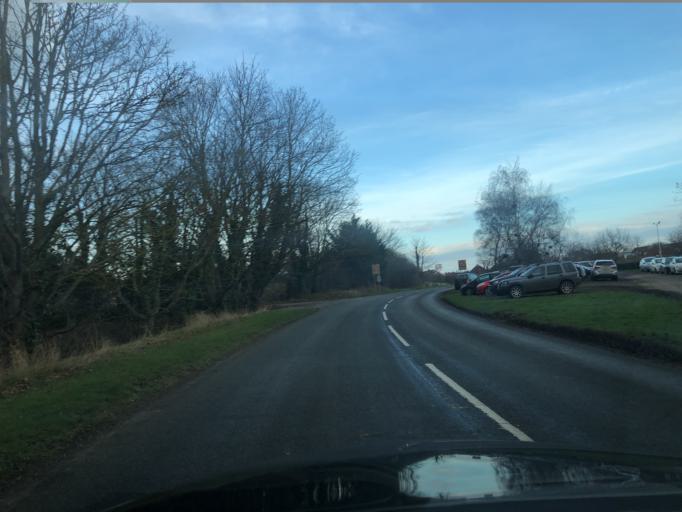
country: GB
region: England
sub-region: North Yorkshire
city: Bedale
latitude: 54.2821
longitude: -1.6010
